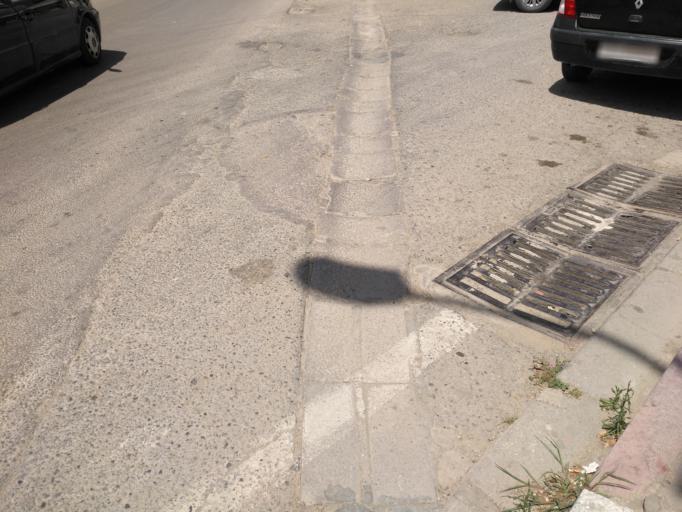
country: TN
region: Silyanah
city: Siliana
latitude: 36.0849
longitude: 9.3692
